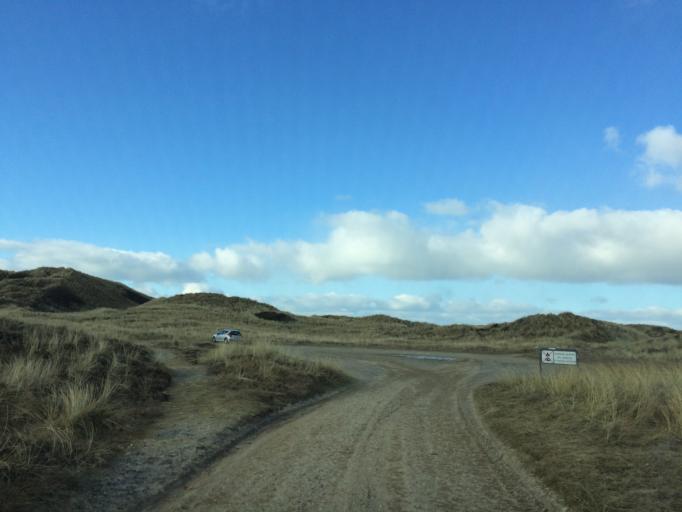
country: DK
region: Central Jutland
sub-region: Holstebro Kommune
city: Ulfborg
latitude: 56.2772
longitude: 8.1327
